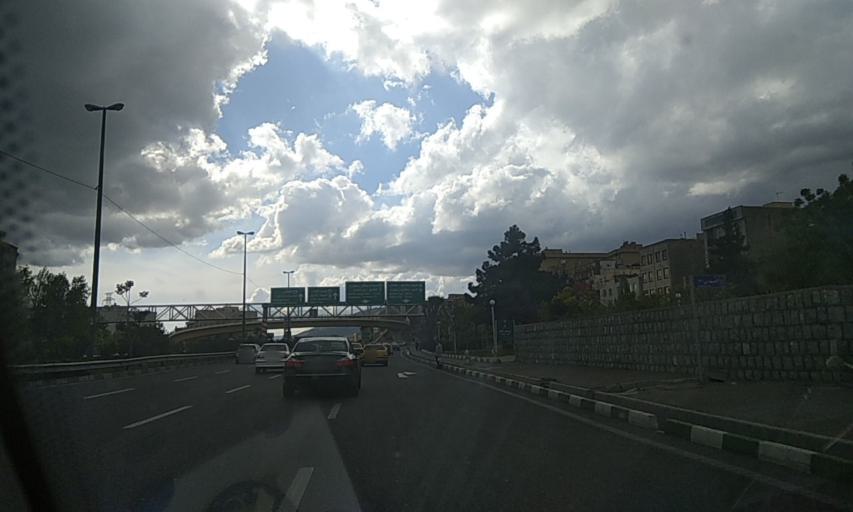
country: IR
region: Tehran
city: Tajrish
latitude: 35.7702
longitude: 51.3255
